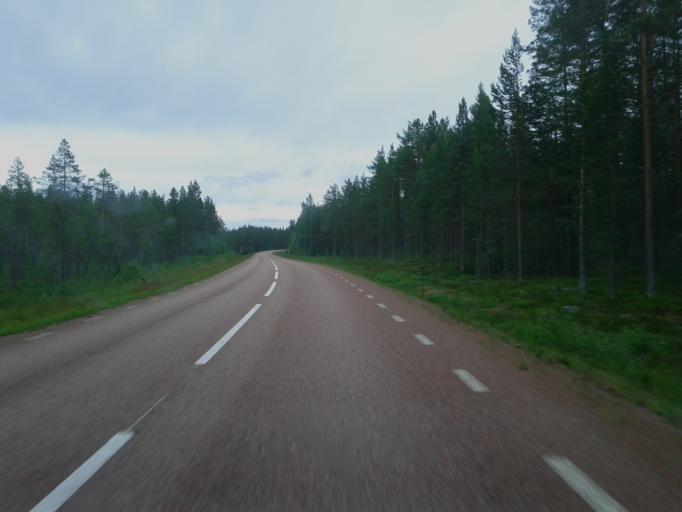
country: SE
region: Dalarna
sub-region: Alvdalens Kommun
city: AElvdalen
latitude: 61.5268
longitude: 13.3592
